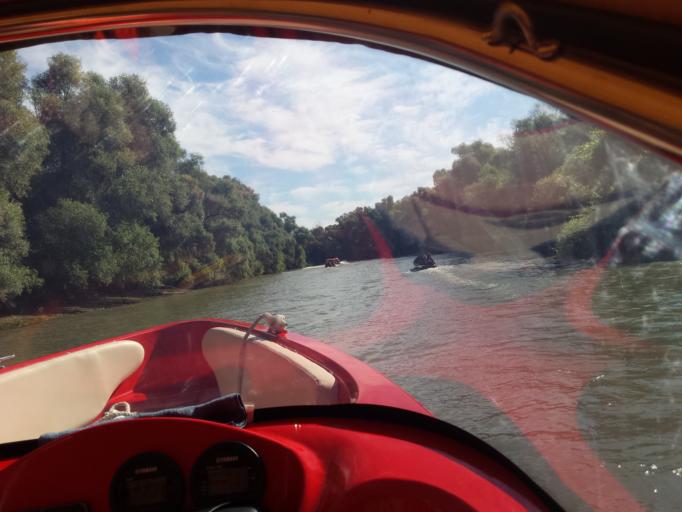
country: RO
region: Tulcea
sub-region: Comuna Pardina
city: Pardina
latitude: 45.2558
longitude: 28.9408
